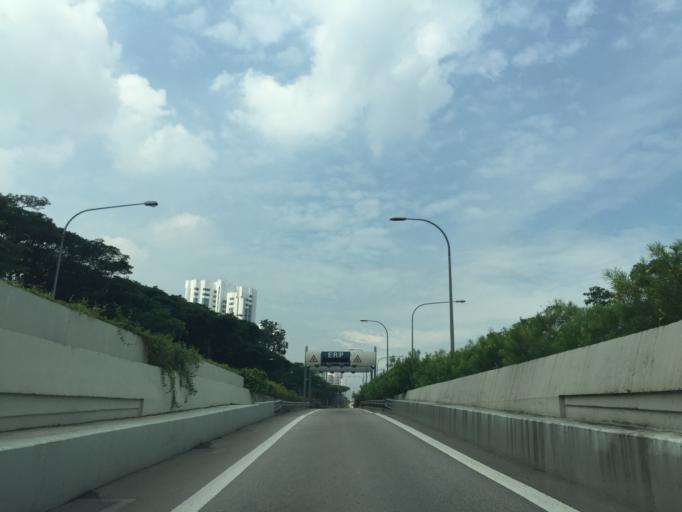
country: SG
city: Singapore
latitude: 1.2958
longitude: 103.8792
